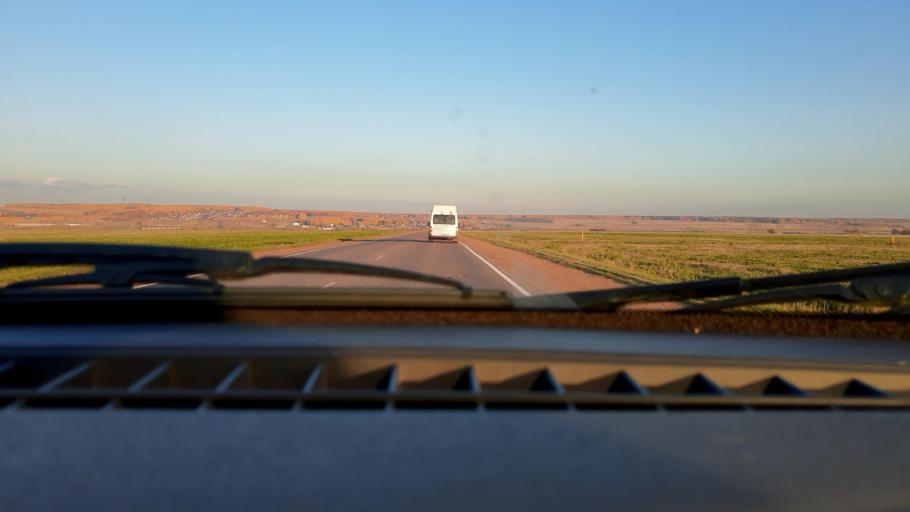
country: RU
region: Bashkortostan
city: Avdon
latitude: 54.8238
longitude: 55.6534
